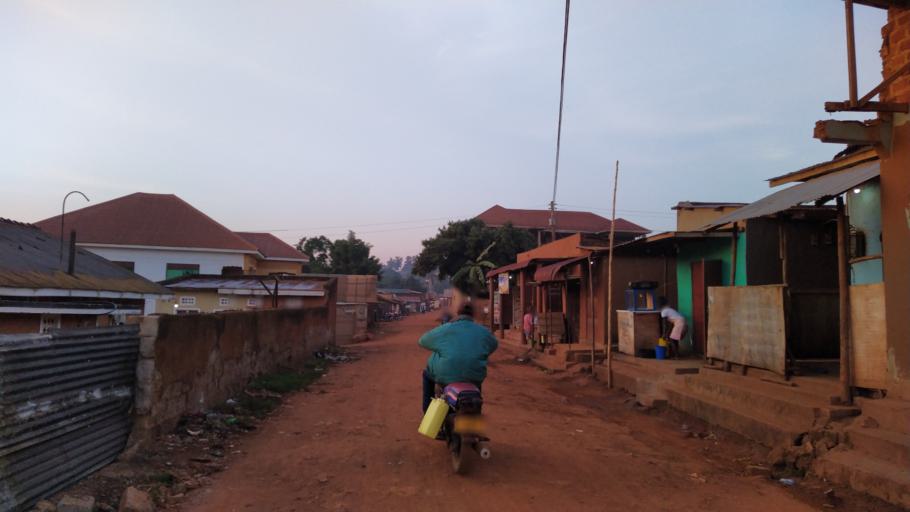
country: UG
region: Central Region
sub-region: Kampala District
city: Kampala
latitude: 0.2743
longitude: 32.5734
